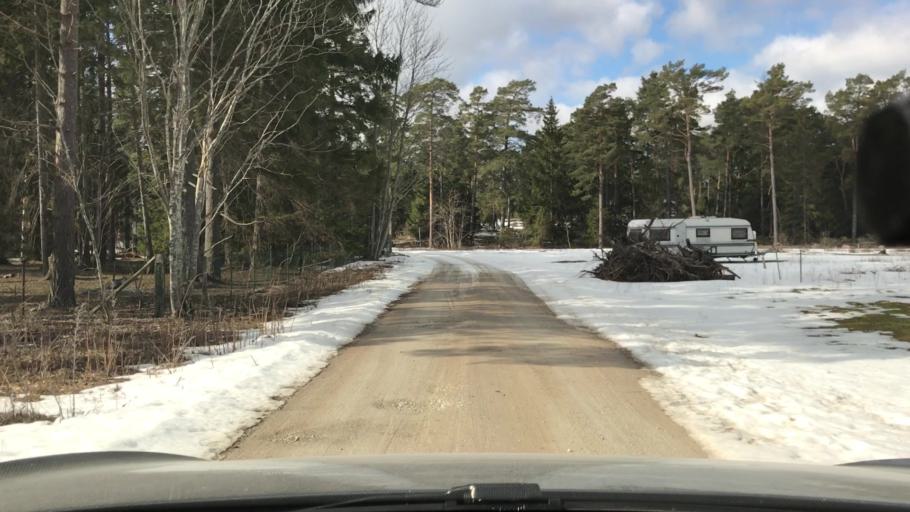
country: SE
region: Gotland
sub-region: Gotland
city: Slite
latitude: 57.3452
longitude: 18.7293
